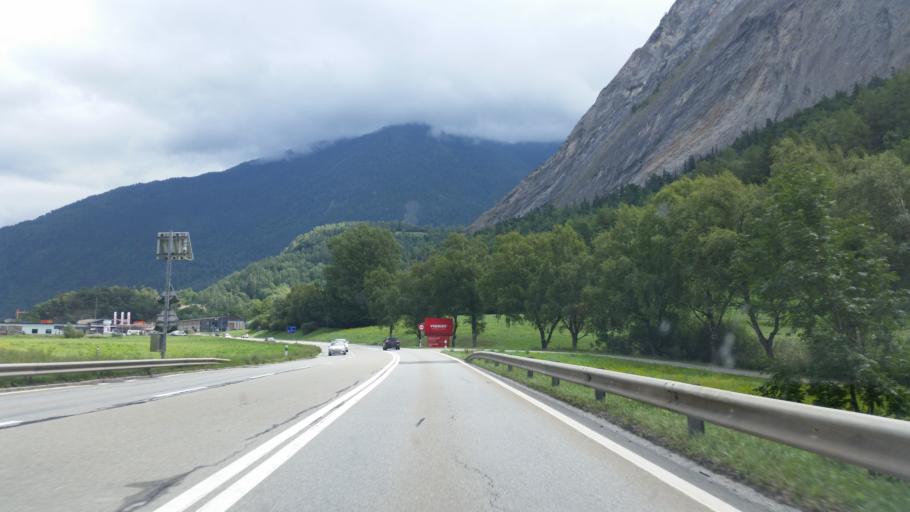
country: CH
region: Valais
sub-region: Martigny District
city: Charrat-les-Chenes
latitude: 46.0787
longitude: 7.1323
